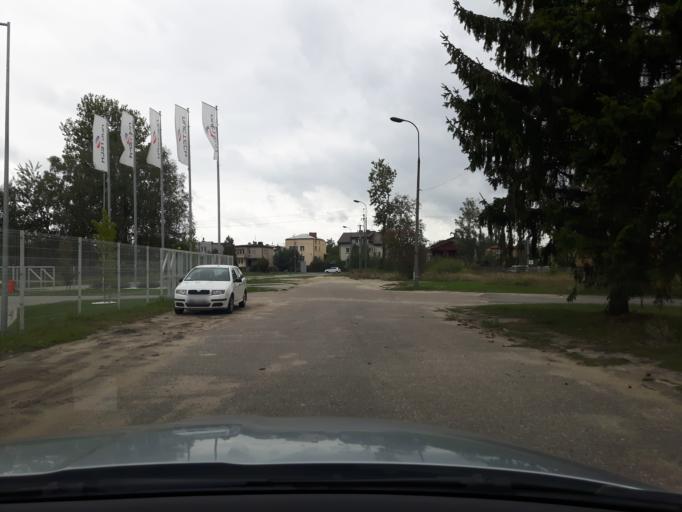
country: PL
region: Masovian Voivodeship
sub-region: Powiat wolominski
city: Kobylka
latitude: 52.3304
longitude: 21.1946
